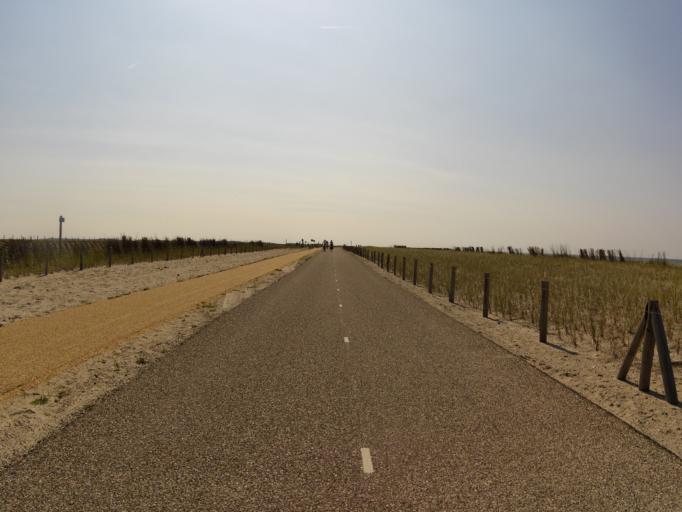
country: NL
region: North Holland
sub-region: Gemeente Schagen
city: Harenkarspel
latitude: 52.7579
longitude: 4.6499
